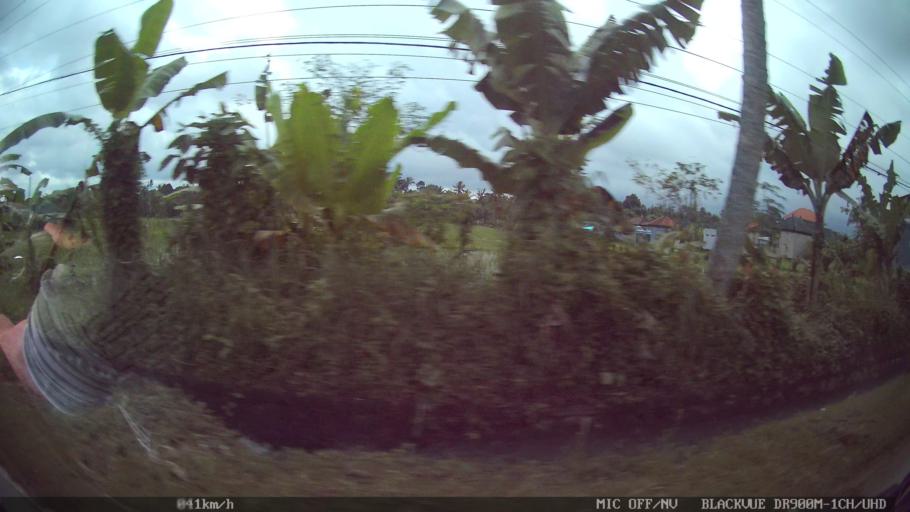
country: ID
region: Bali
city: Pohgending Kawan
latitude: -8.4431
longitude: 115.1408
